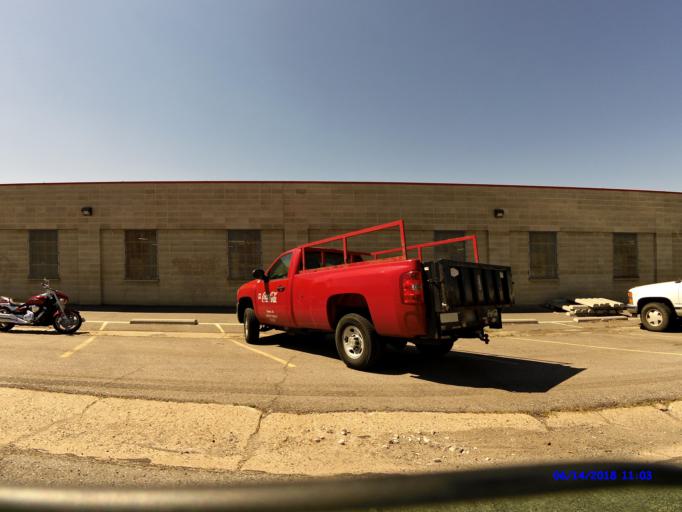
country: US
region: Utah
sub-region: Weber County
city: Ogden
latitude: 41.2134
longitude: -112.0054
